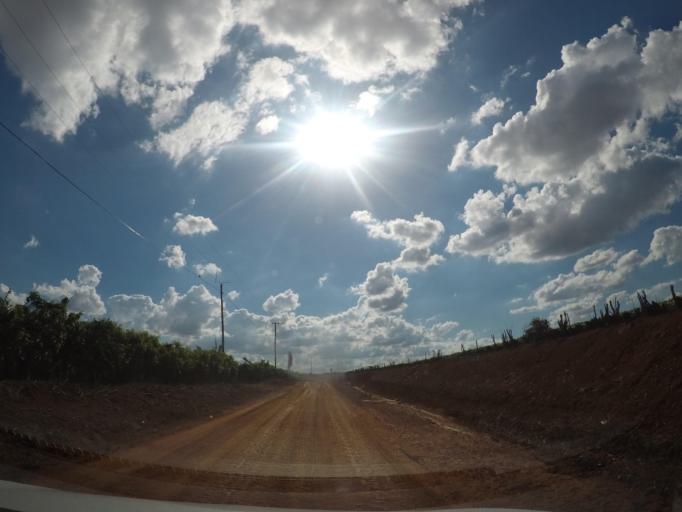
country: BR
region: Sao Paulo
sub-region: Sumare
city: Sumare
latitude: -22.8446
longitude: -47.3104
